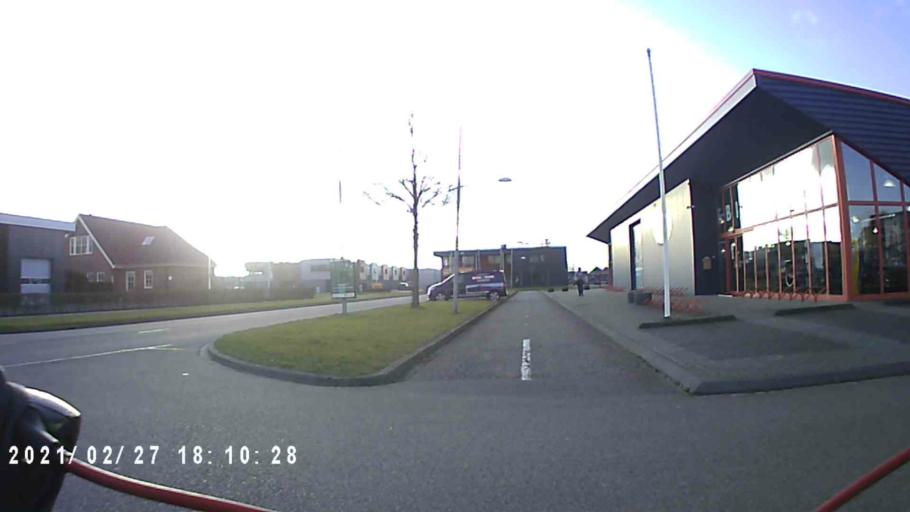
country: NL
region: Groningen
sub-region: Gemeente Bedum
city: Bedum
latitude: 53.2936
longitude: 6.5966
